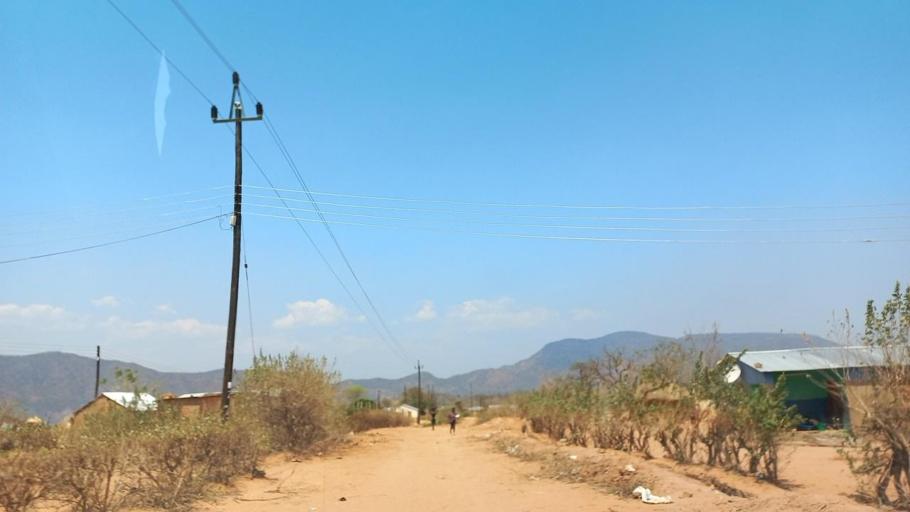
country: ZM
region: Lusaka
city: Luangwa
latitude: -15.5904
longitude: 30.3910
